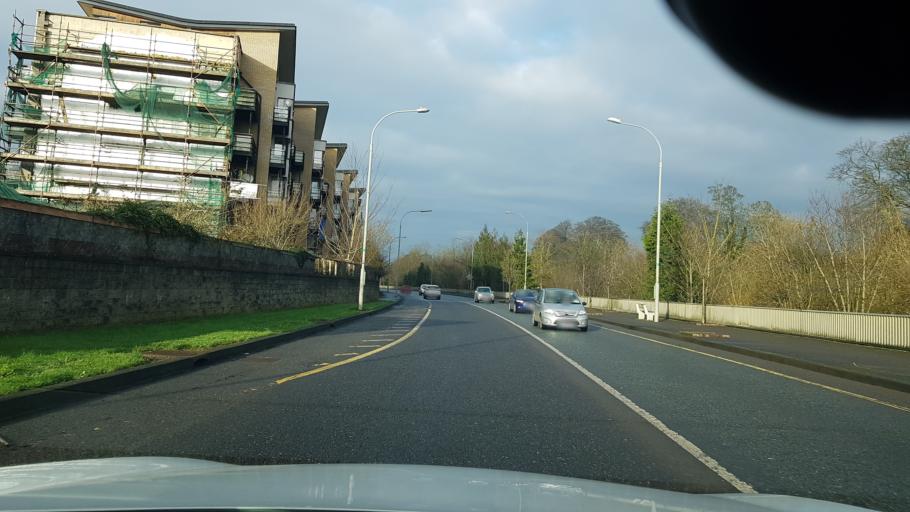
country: IE
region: Leinster
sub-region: An Mhi
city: Navan
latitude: 53.6459
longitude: -6.6740
